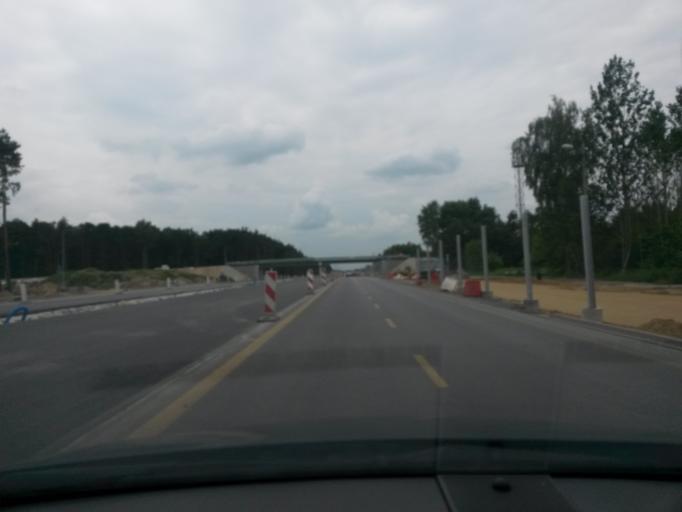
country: PL
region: Masovian Voivodeship
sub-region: Powiat pruszkowski
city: Komorow
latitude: 52.1140
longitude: 20.8561
